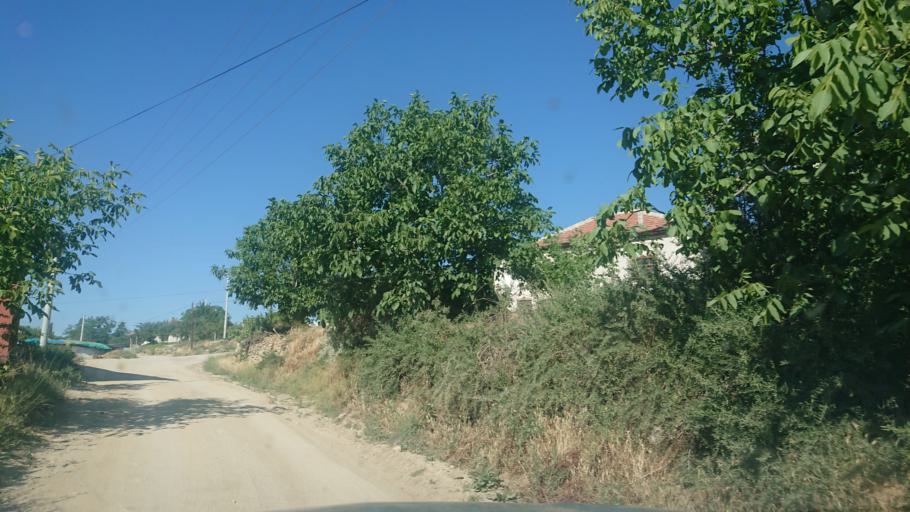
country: TR
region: Aksaray
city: Agacoren
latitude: 38.9040
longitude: 33.8592
